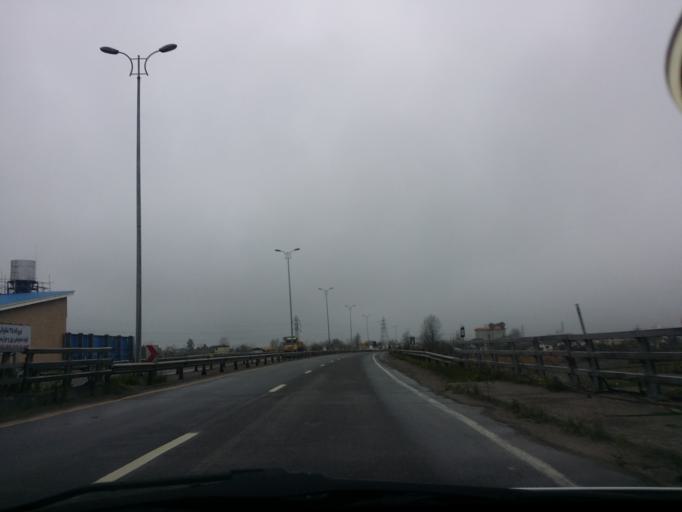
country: IR
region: Mazandaran
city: Tonekabon
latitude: 36.8098
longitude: 50.8610
